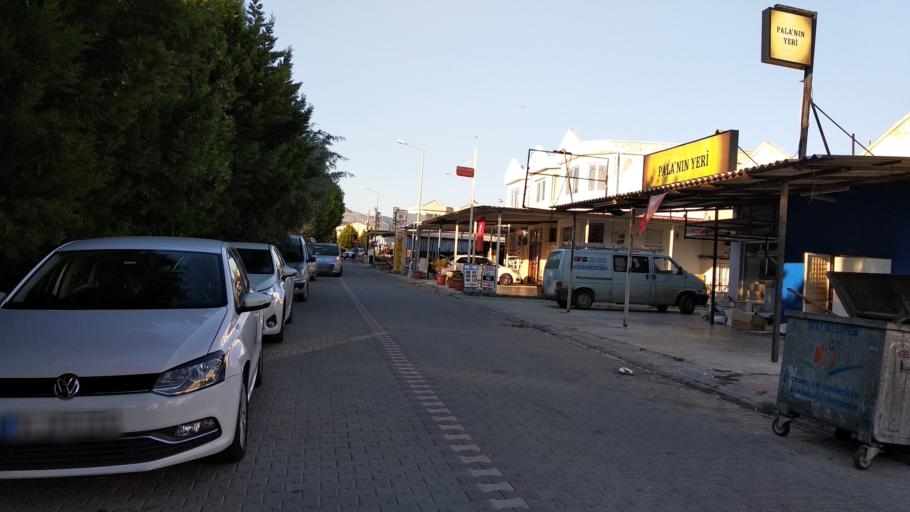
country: TR
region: Balikesir
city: Altinova
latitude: 39.1578
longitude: 26.8215
